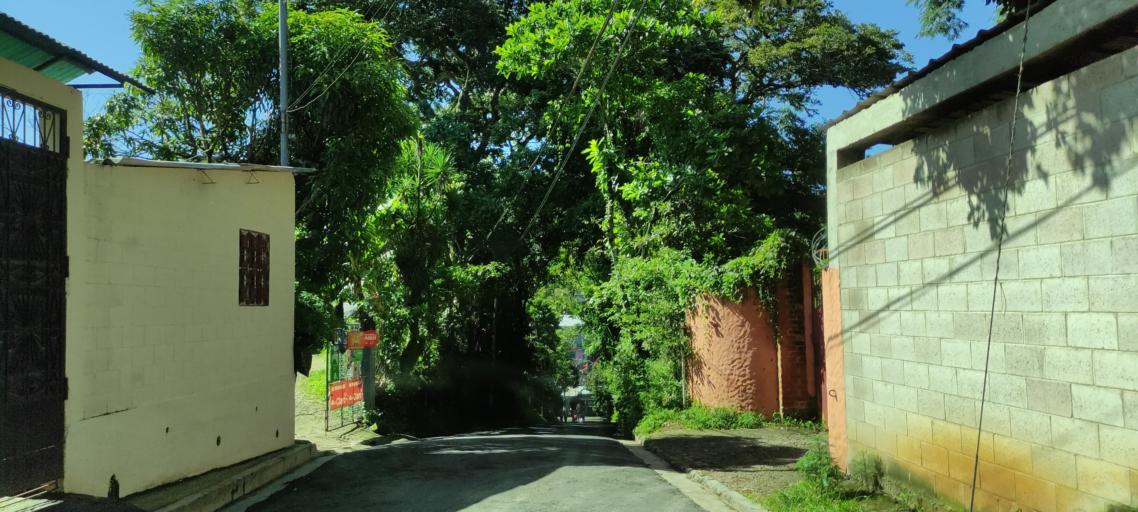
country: HN
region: Ocotepeque
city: Antigua Ocotepeque
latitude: 14.3162
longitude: -89.1738
